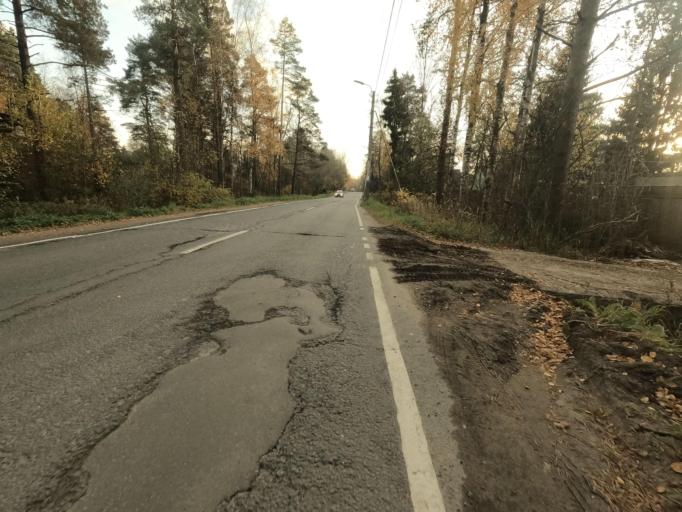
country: RU
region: St.-Petersburg
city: Beloostrov
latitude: 60.1627
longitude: 30.0074
